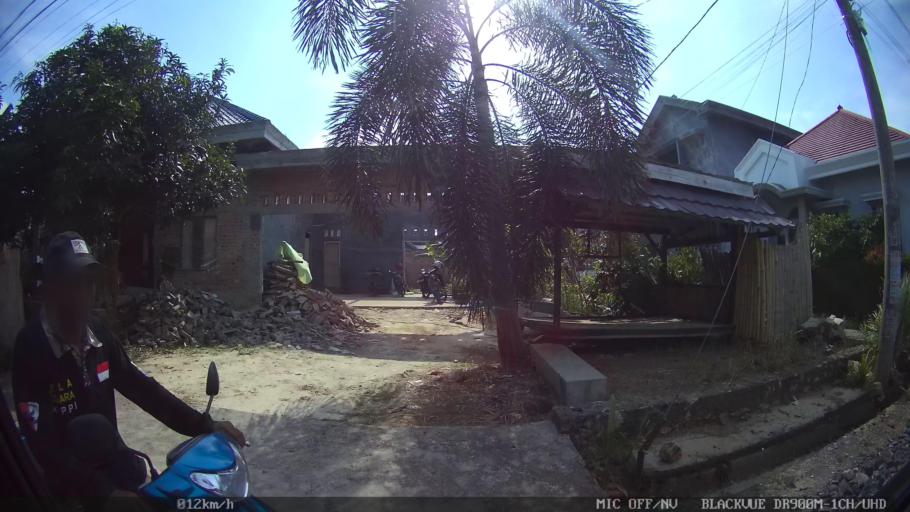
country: ID
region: Lampung
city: Kedaton
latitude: -5.3812
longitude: 105.2407
